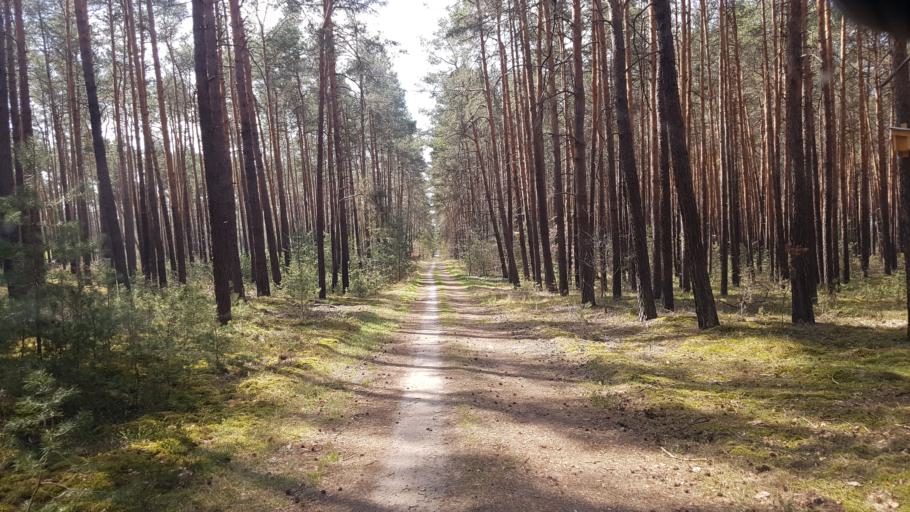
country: DE
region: Brandenburg
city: Finsterwalde
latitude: 51.5681
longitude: 13.6794
